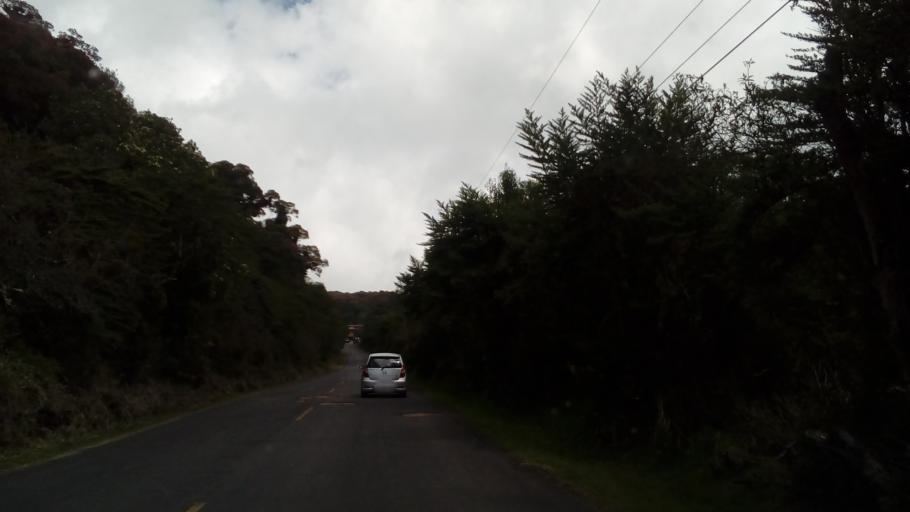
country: CR
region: Alajuela
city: Rio Segundo
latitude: 10.1777
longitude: -84.2377
